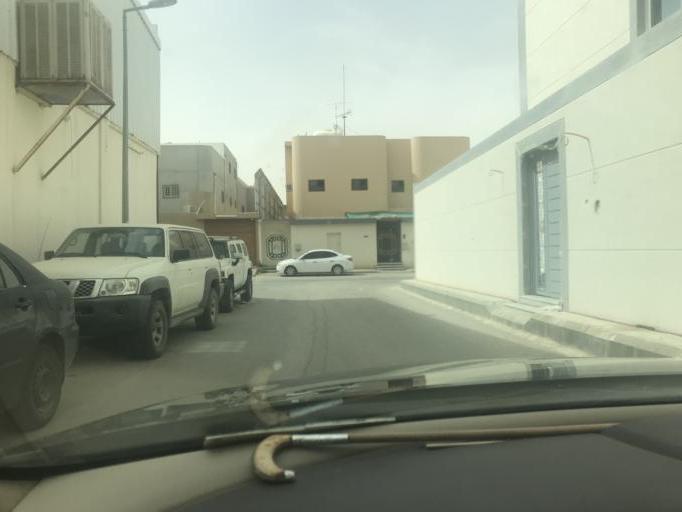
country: SA
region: Ar Riyad
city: Riyadh
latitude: 24.7910
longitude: 46.6915
